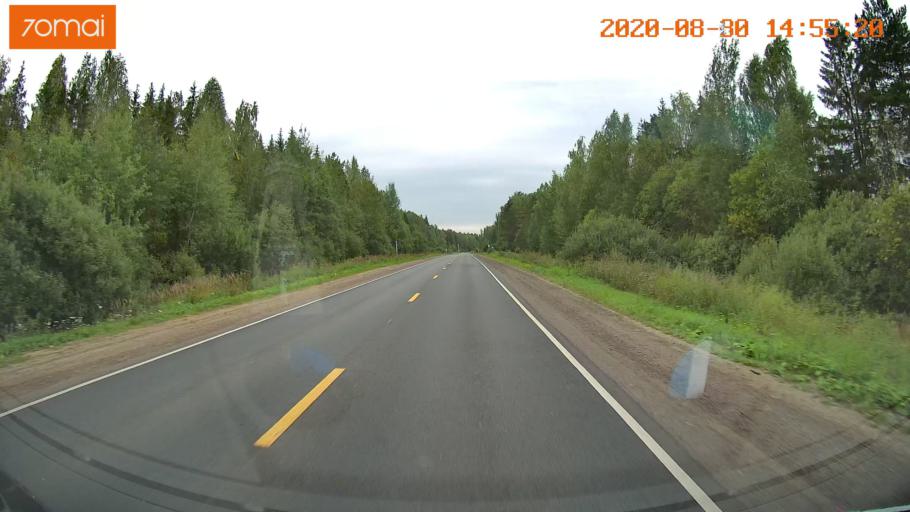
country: RU
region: Ivanovo
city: Kineshma
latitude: 57.3856
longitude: 42.0372
